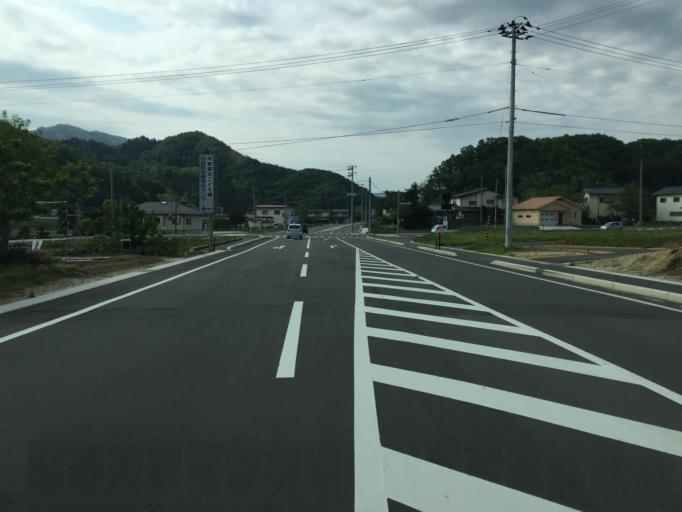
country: JP
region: Fukushima
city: Hobaramachi
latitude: 37.7315
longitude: 140.6041
